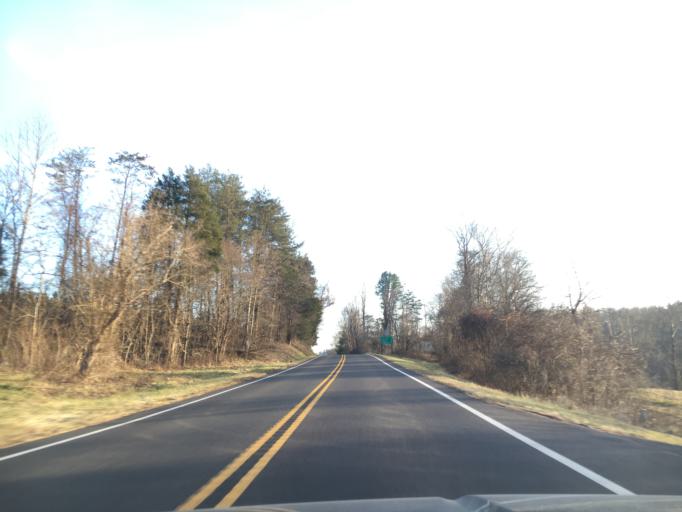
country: US
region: Virginia
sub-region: Rappahannock County
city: Washington
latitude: 38.5944
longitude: -78.1678
